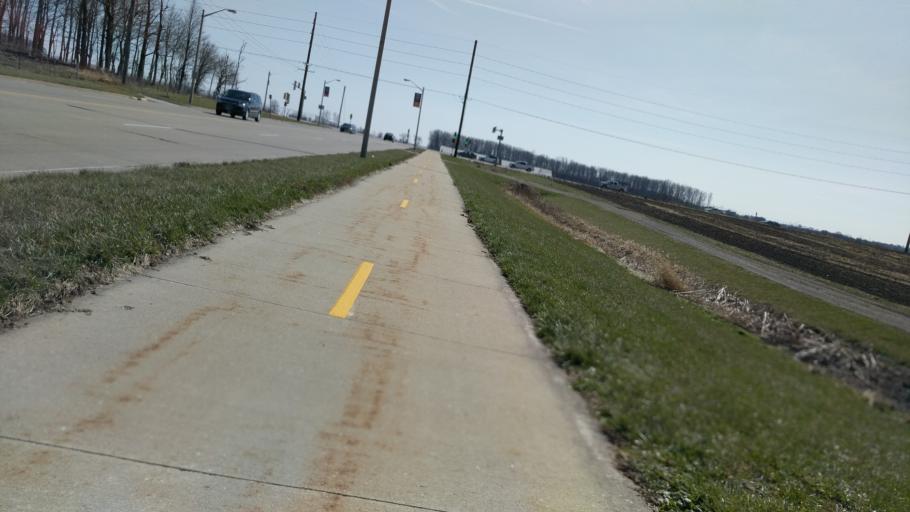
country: US
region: Illinois
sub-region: Champaign County
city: Urbana
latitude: 40.0849
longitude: -88.2190
